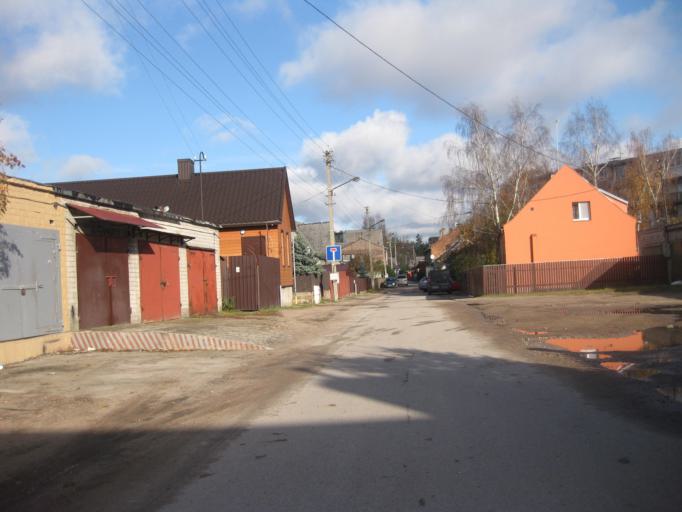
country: LT
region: Kauno apskritis
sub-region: Kaunas
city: Kaunas
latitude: 54.9073
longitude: 23.8903
